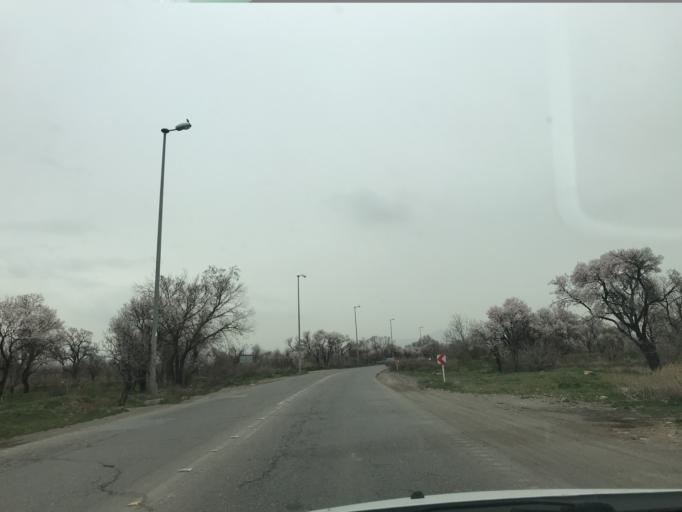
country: IR
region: Qazvin
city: Qazvin
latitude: 36.2775
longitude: 49.9795
